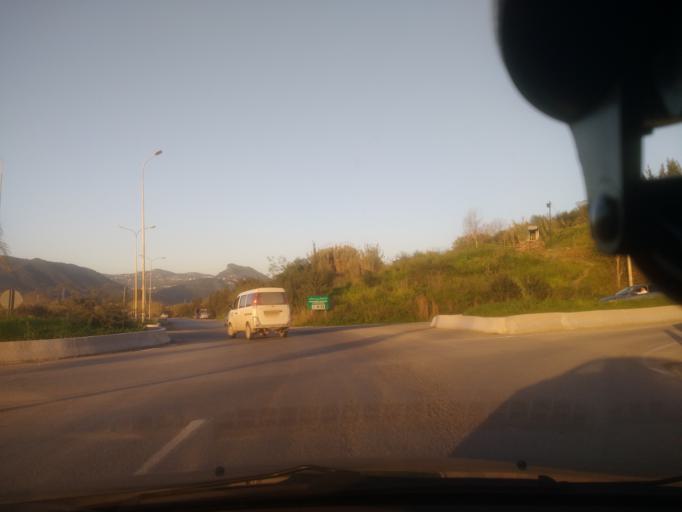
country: DZ
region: Tizi Ouzou
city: Tizi Ouzou
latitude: 36.7474
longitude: 4.0140
